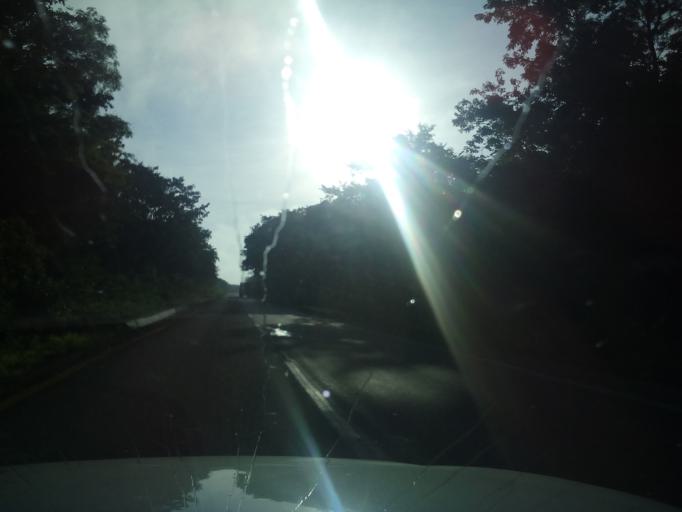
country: MX
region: Yucatan
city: Tunkas
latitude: 20.7660
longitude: -88.8055
